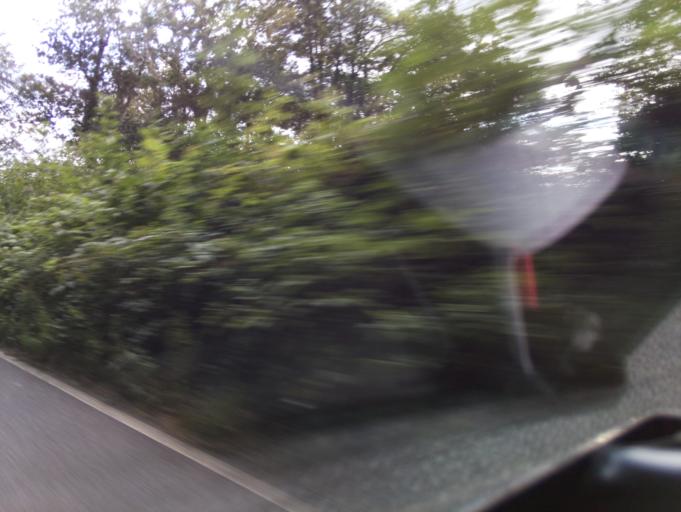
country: GB
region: England
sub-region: Devon
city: Honiton
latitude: 50.7461
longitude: -3.2088
